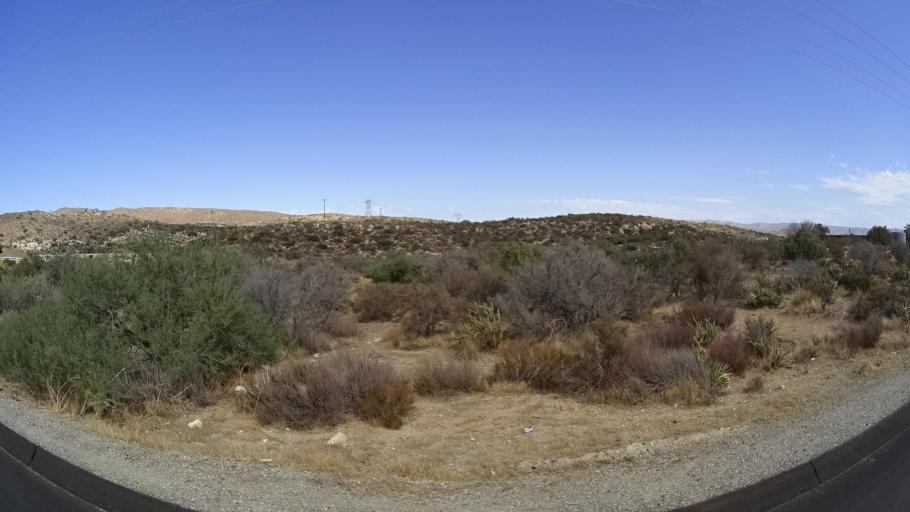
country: MX
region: Baja California
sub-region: Tecate
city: Cereso del Hongo
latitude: 32.6344
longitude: -116.2261
